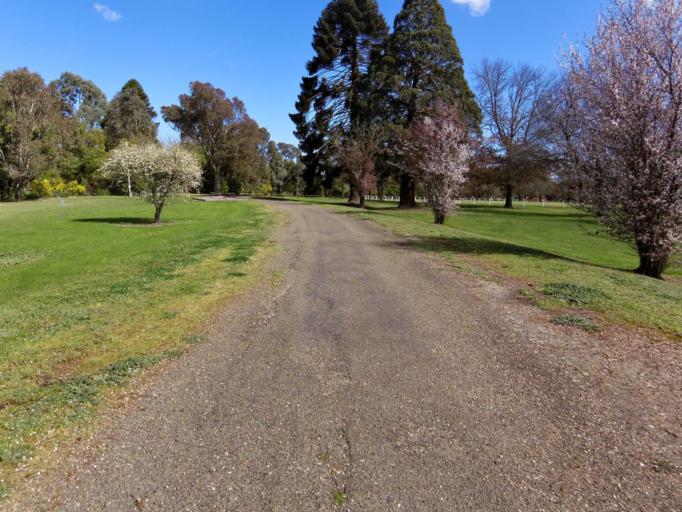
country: AU
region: Victoria
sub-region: Murrindindi
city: Alexandra
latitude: -37.1871
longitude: 145.7148
